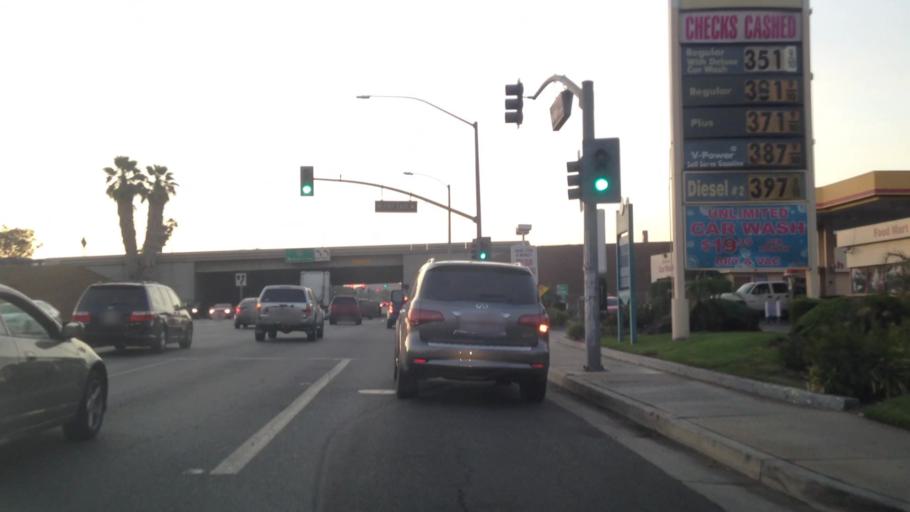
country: US
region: California
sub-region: Riverside County
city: Home Gardens
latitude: 33.8853
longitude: -117.5169
